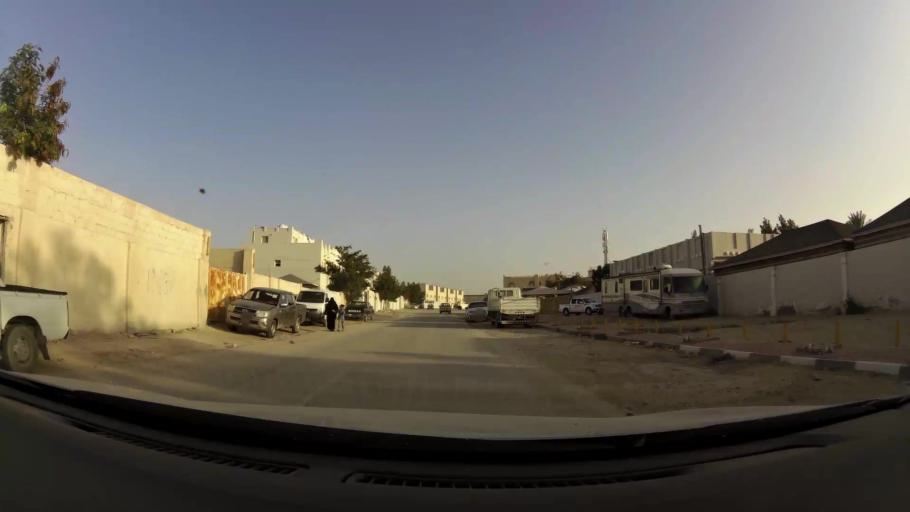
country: QA
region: Baladiyat ar Rayyan
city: Ar Rayyan
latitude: 25.3257
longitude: 51.4520
